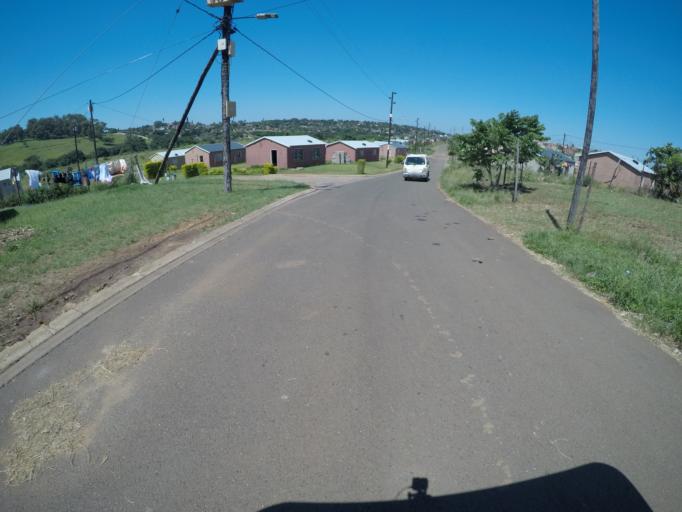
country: ZA
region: KwaZulu-Natal
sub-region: uThungulu District Municipality
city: Empangeni
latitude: -28.7629
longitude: 31.8781
